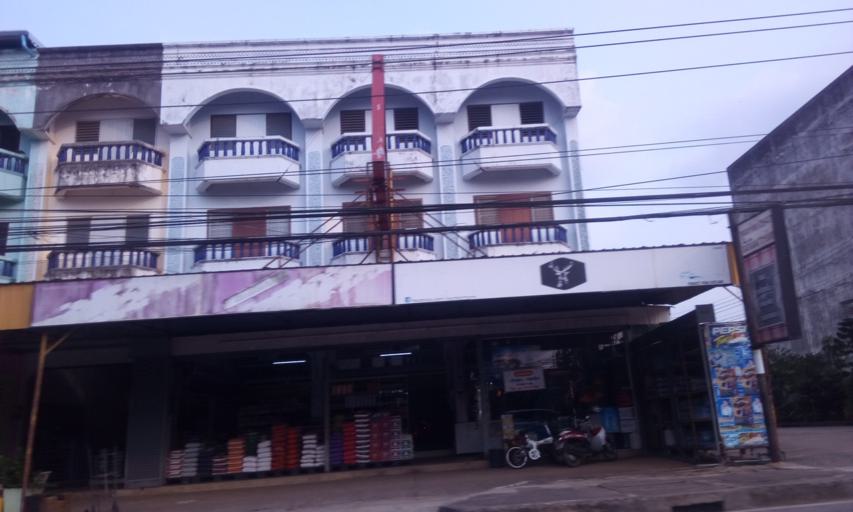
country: TH
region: Trat
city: Khao Saming
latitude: 12.3697
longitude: 102.3876
